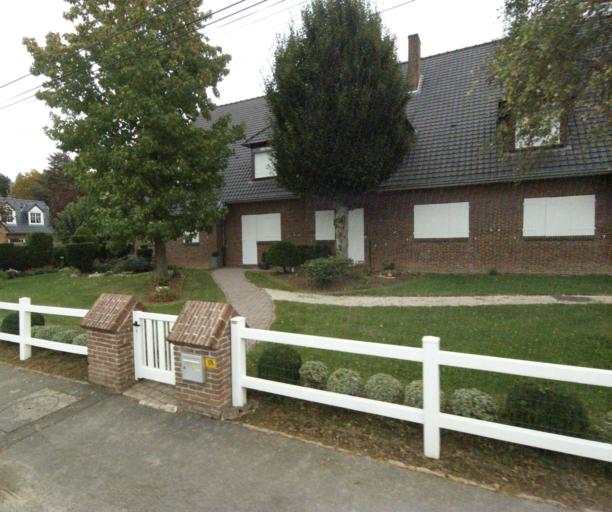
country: FR
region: Nord-Pas-de-Calais
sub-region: Departement du Nord
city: Houplines
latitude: 50.6627
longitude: 2.9104
